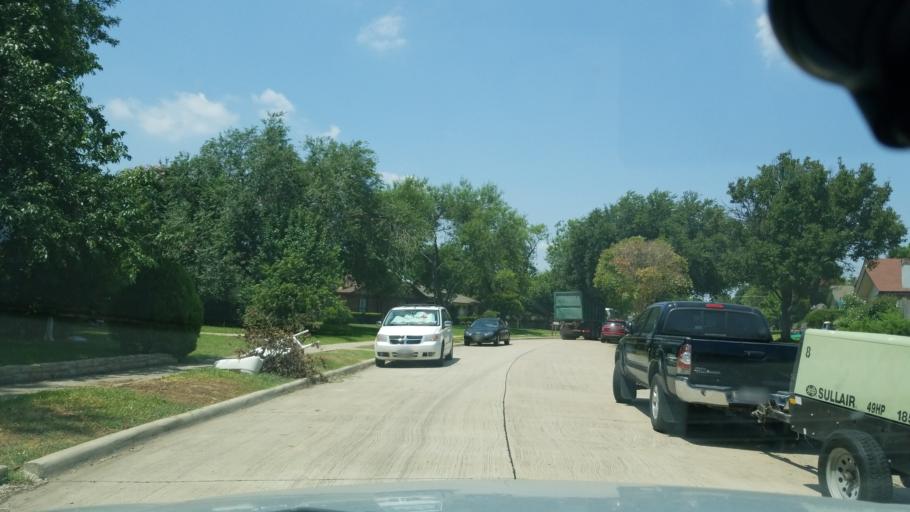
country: US
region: Texas
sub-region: Dallas County
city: Carrollton
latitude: 32.9507
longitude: -96.8808
